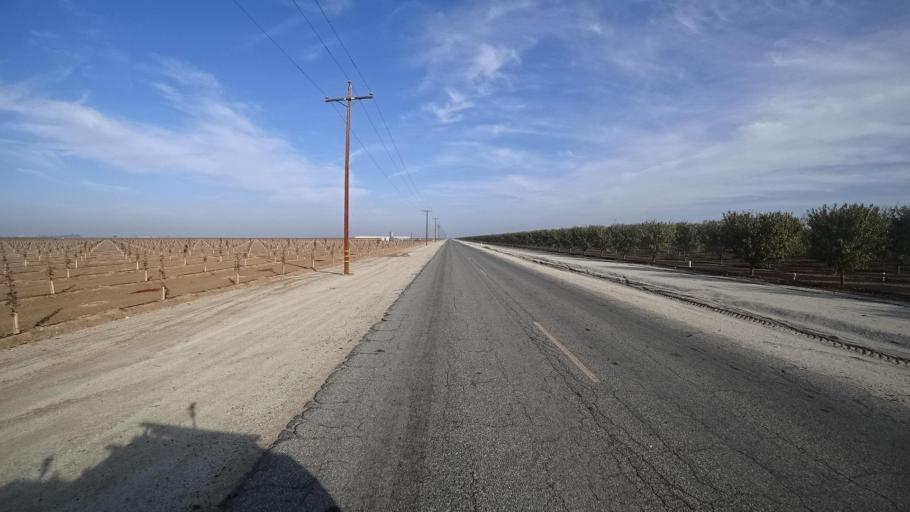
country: US
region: California
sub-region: Kern County
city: McFarland
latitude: 35.6906
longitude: -119.2049
